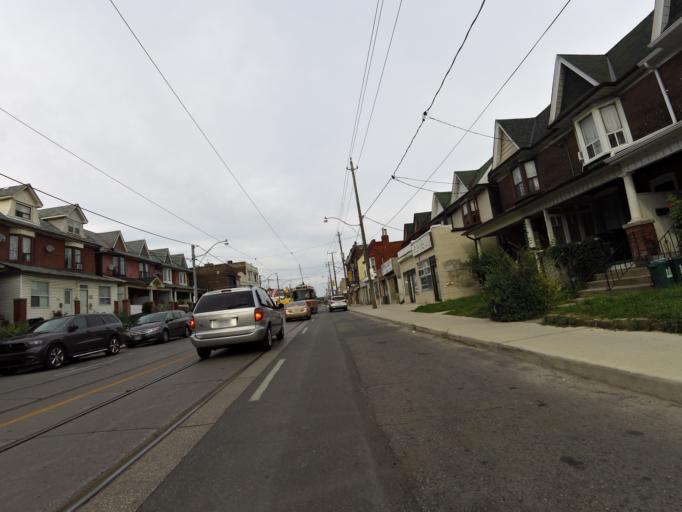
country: CA
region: Ontario
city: Toronto
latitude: 43.6706
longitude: -79.3292
